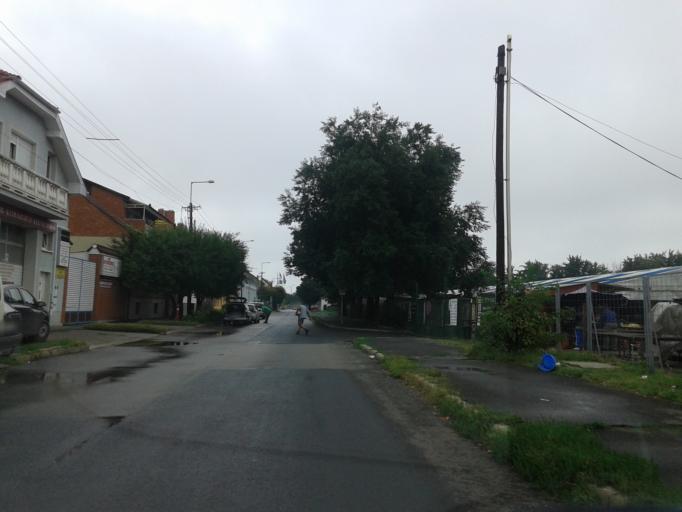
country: HU
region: Csongrad
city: Szeged
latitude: 46.2448
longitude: 20.1268
